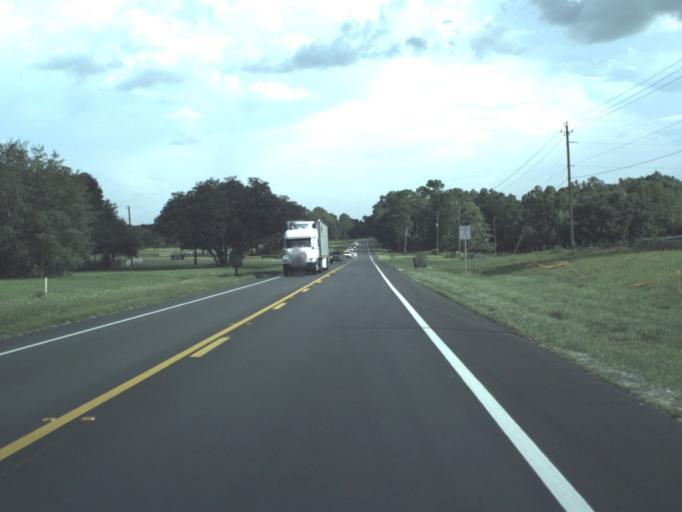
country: US
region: Florida
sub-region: Polk County
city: Polk City
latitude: 28.2933
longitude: -81.8336
